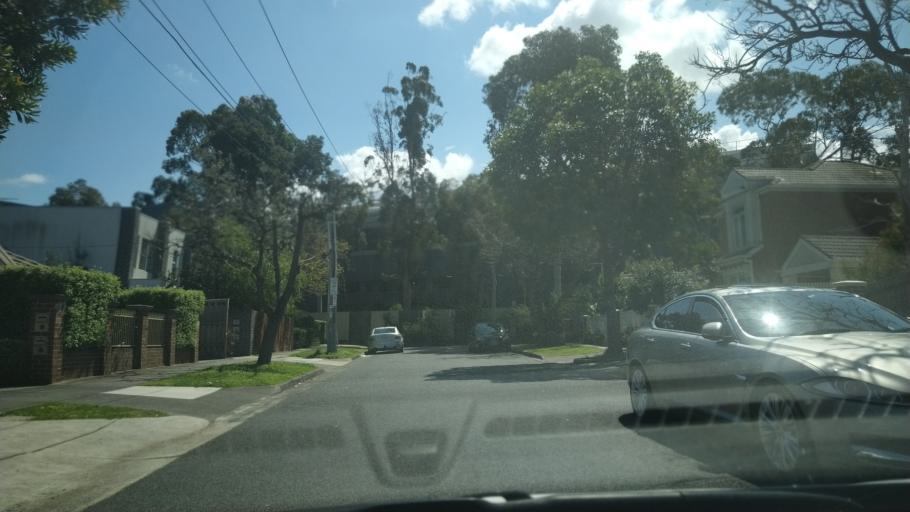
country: AU
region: Victoria
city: Highett
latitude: -37.9598
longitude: 145.0522
